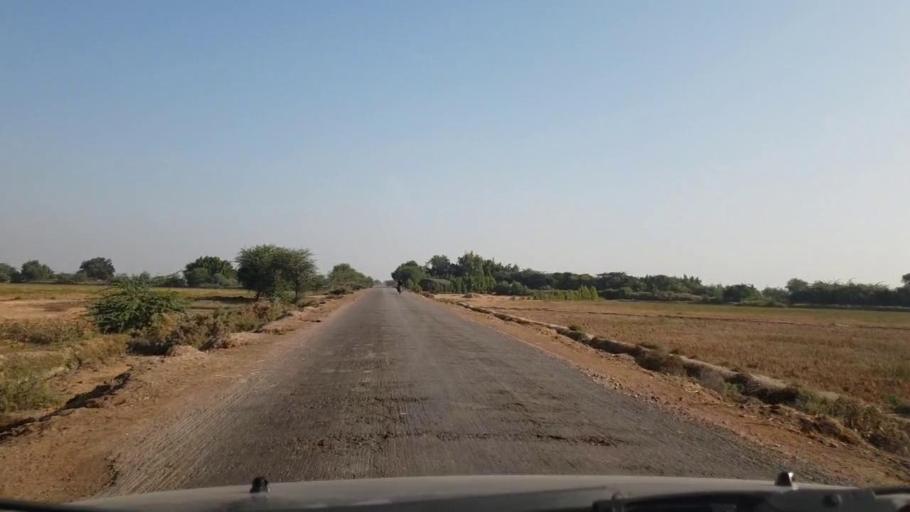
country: PK
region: Sindh
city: Tando Bago
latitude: 24.8598
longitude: 69.0455
